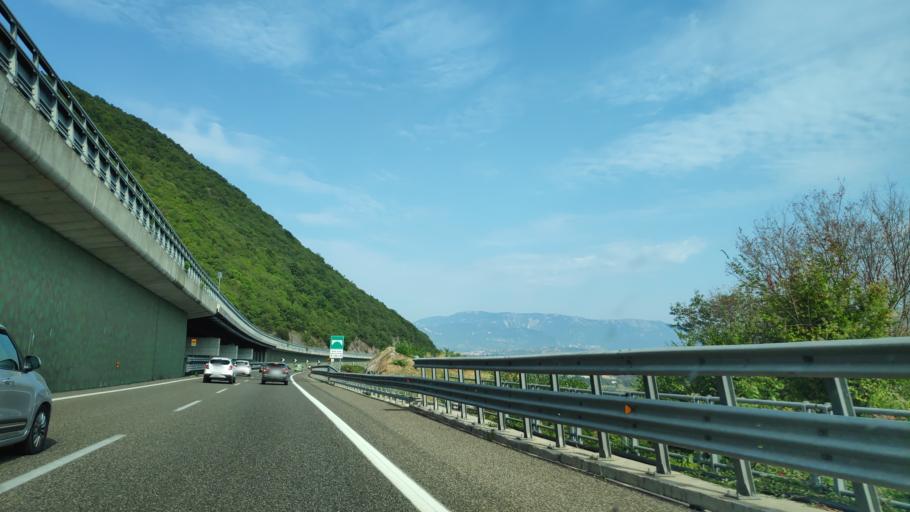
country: IT
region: Campania
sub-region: Provincia di Salerno
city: Sicignano degli Alburni
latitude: 40.5916
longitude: 15.3279
